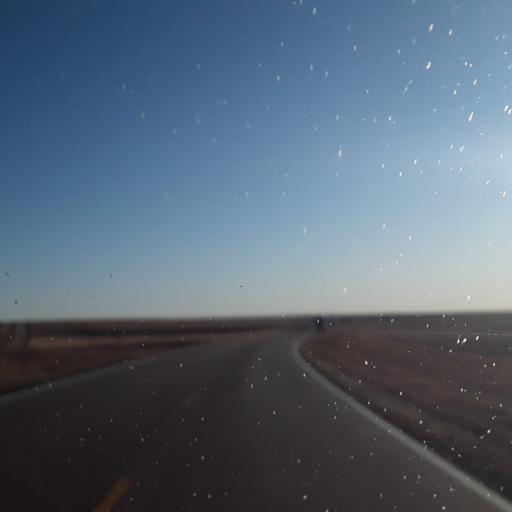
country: US
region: Kansas
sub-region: Wallace County
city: Sharon Springs
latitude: 39.1137
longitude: -101.7285
